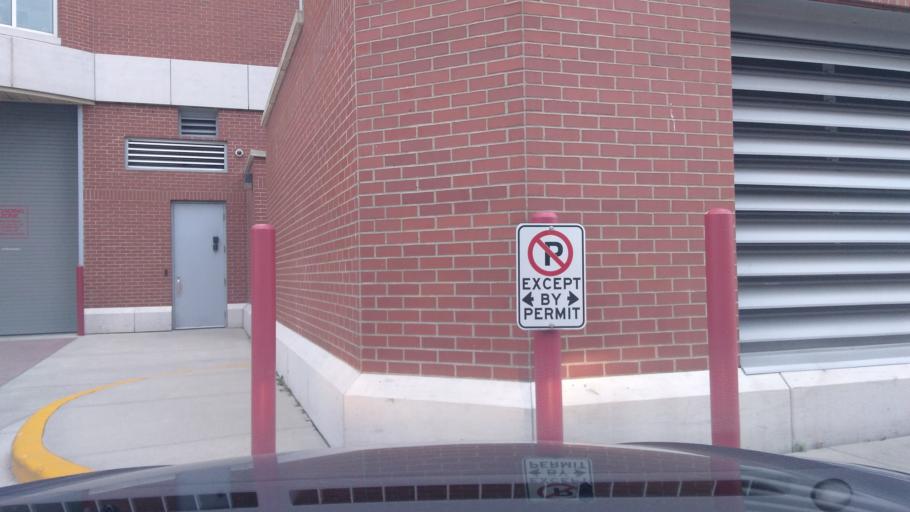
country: CA
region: Alberta
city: Calgary
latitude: 51.0416
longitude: -114.0544
